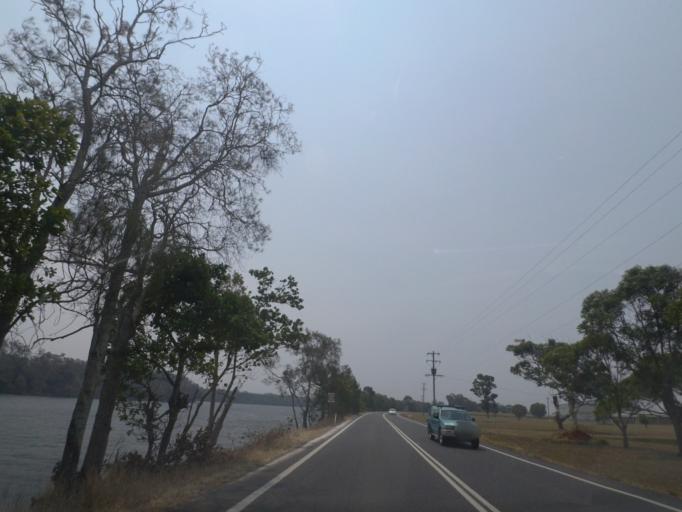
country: AU
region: New South Wales
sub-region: Richmond Valley
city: Evans Head
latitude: -28.9868
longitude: 153.4623
